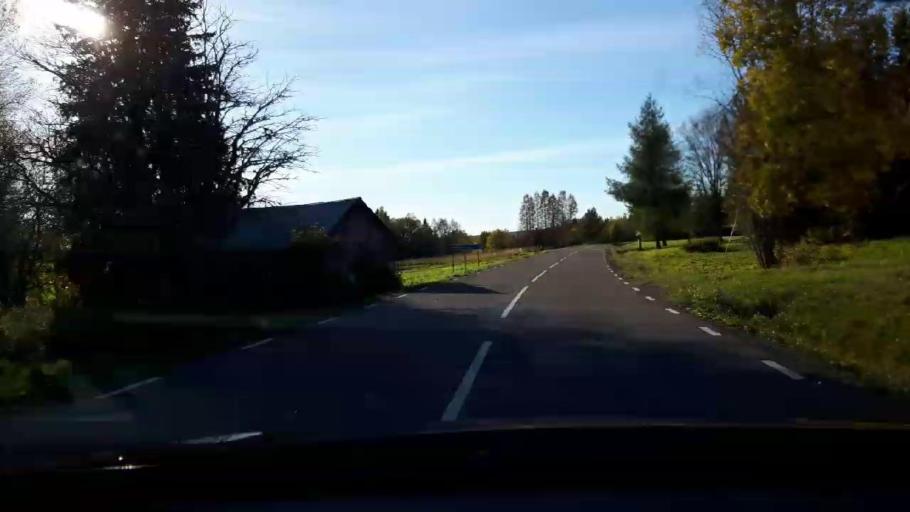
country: SE
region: Jaemtland
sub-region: Stroemsunds Kommun
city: Stroemsund
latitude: 63.8658
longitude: 15.1310
